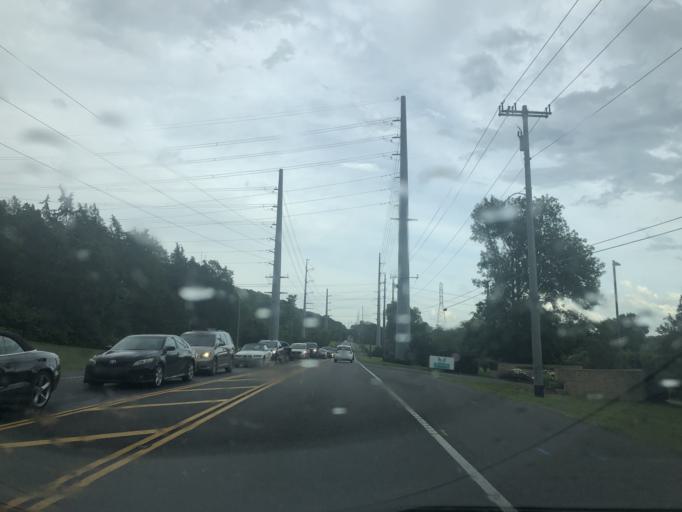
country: US
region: Tennessee
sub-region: Davidson County
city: Forest Hills
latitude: 36.0467
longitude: -86.8605
